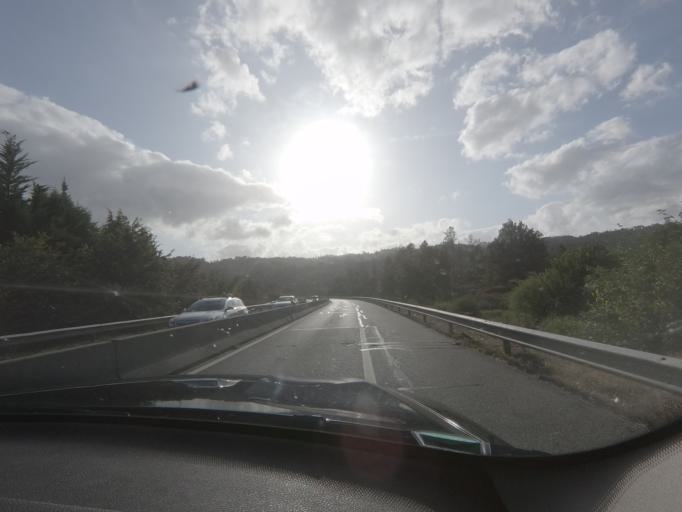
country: PT
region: Viseu
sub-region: Viseu
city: Viseu
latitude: 40.6017
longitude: -7.9910
